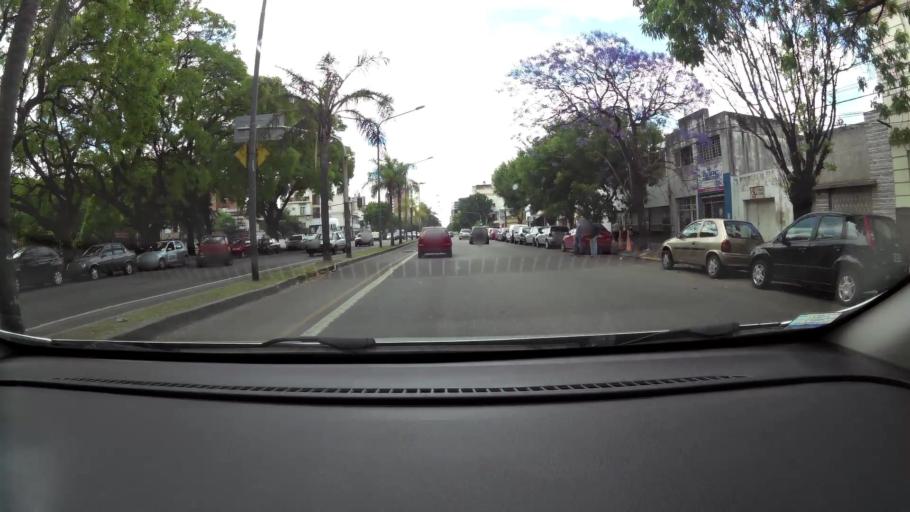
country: AR
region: Santa Fe
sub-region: Departamento de Rosario
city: Rosario
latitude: -32.9653
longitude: -60.6567
